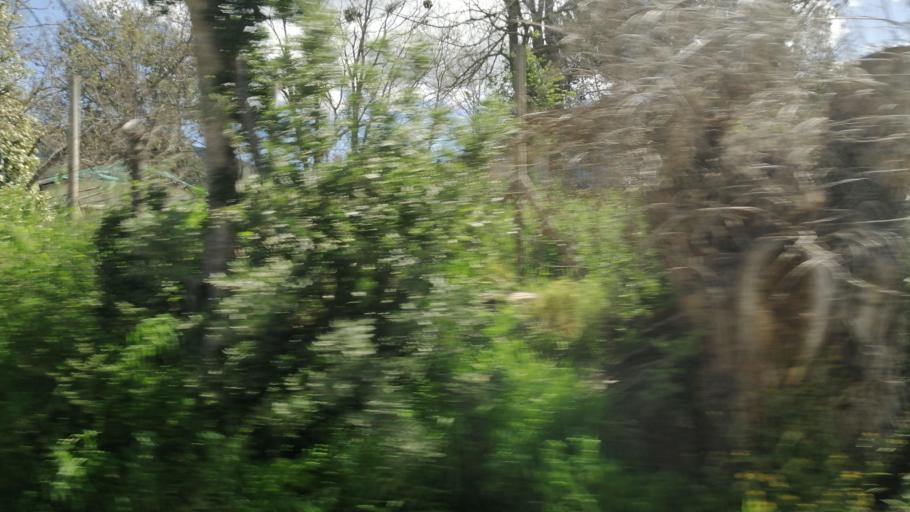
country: CL
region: Valparaiso
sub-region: Provincia de Marga Marga
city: Limache
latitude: -33.1867
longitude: -71.1912
